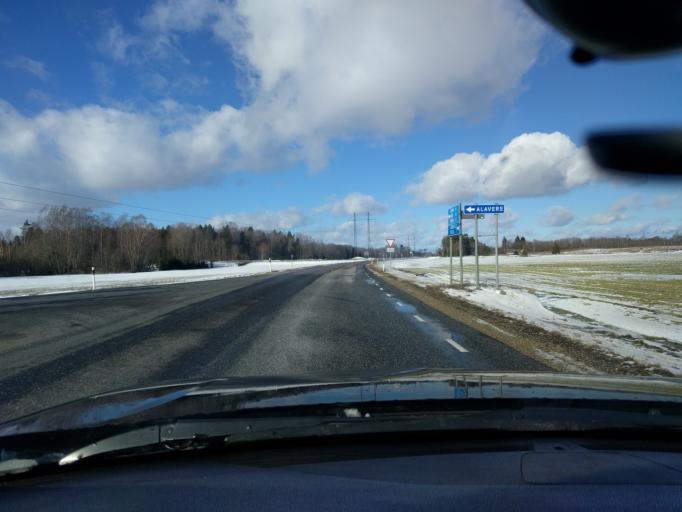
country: EE
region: Harju
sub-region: Anija vald
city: Kehra
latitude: 59.2533
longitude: 25.3279
